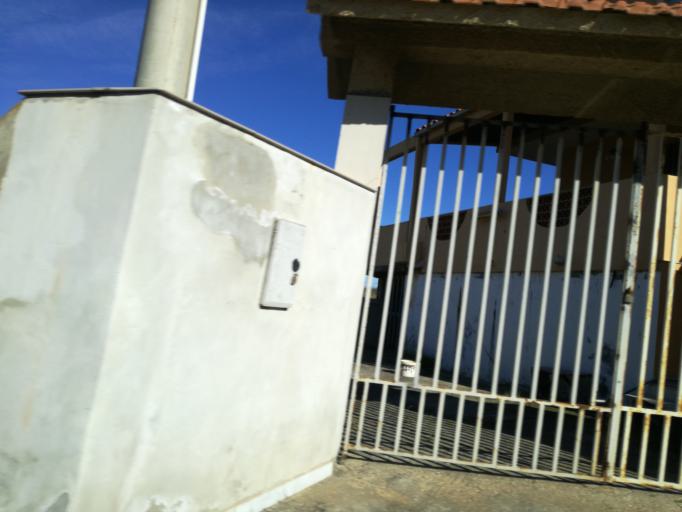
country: IT
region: Sicily
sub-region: Provincia di Caltanissetta
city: Gela
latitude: 37.0914
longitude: 14.1777
